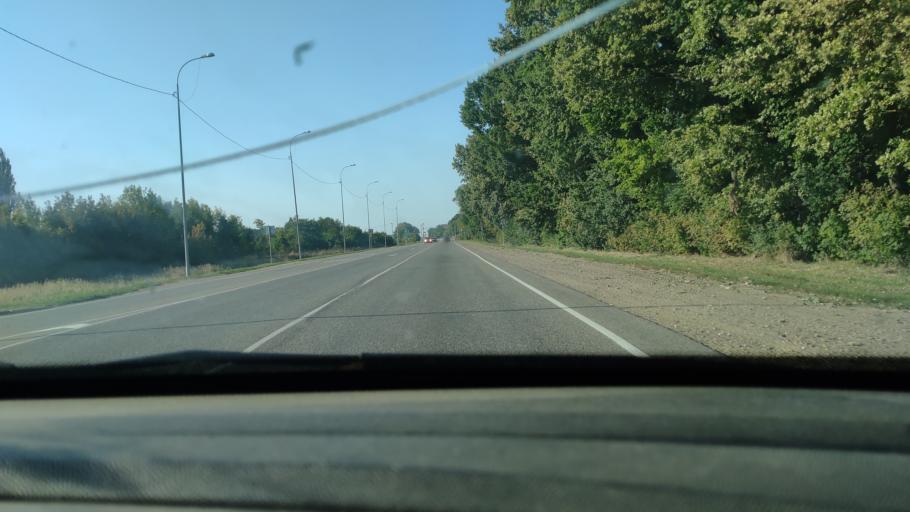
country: RU
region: Krasnodarskiy
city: Medvedovskaya
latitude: 45.4455
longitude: 38.9941
